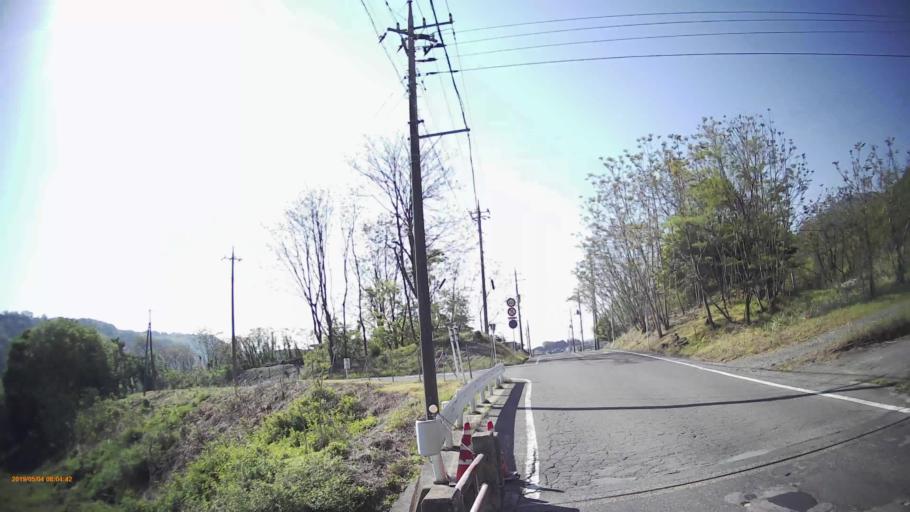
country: JP
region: Yamanashi
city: Nirasaki
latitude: 35.7406
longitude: 138.4069
